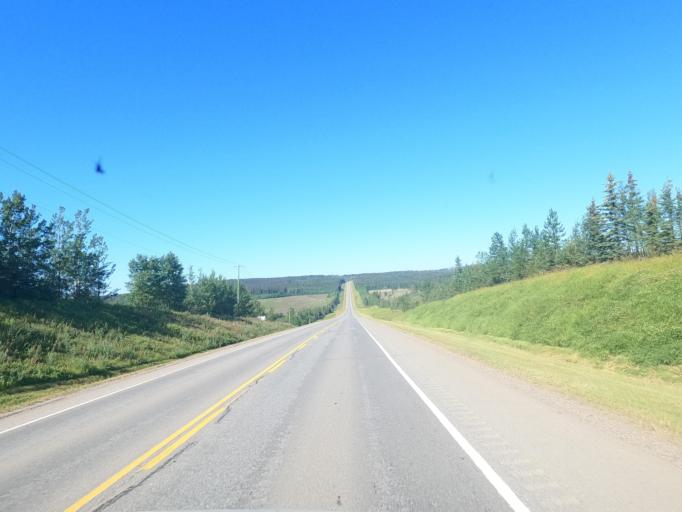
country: CA
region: British Columbia
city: Fort St. John
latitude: 56.6298
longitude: -121.5300
